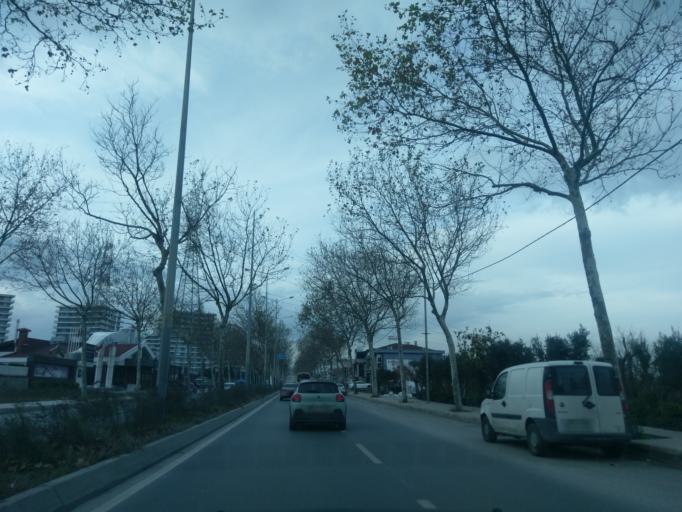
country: TR
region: Istanbul
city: Esenyurt
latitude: 41.0669
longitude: 28.6695
